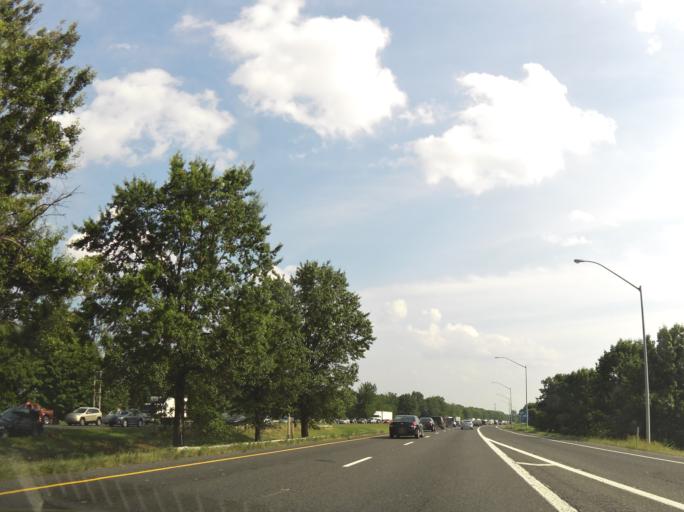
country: US
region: Maryland
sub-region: Washington County
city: Maugansville
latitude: 39.6876
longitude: -77.7333
